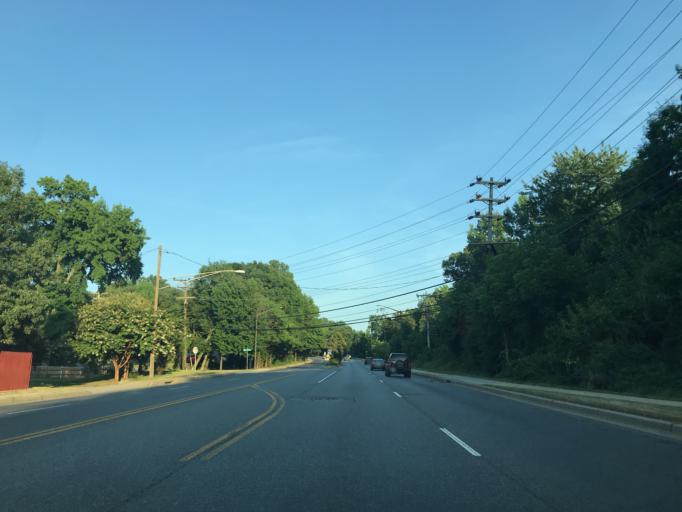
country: US
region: Maryland
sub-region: Anne Arundel County
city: Robinwood
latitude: 38.9538
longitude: -76.5027
